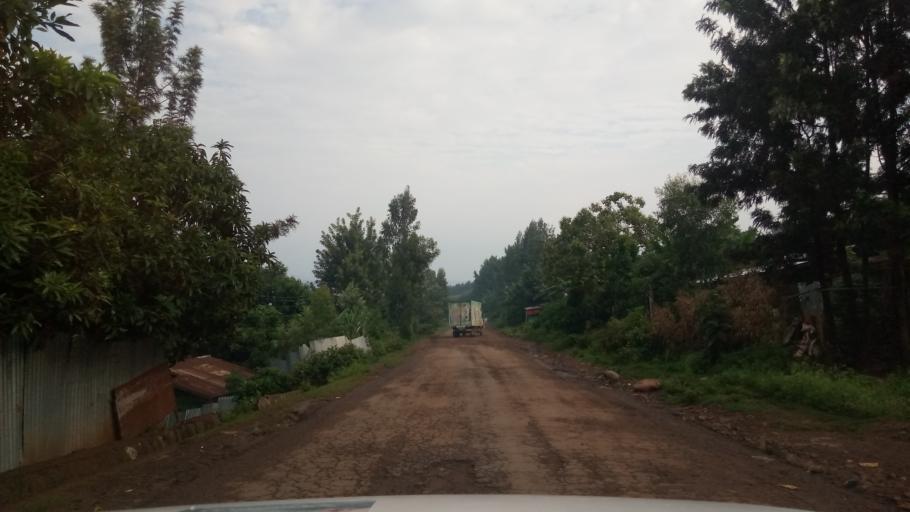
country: ET
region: Oromiya
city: Agaro
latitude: 7.7912
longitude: 36.7262
